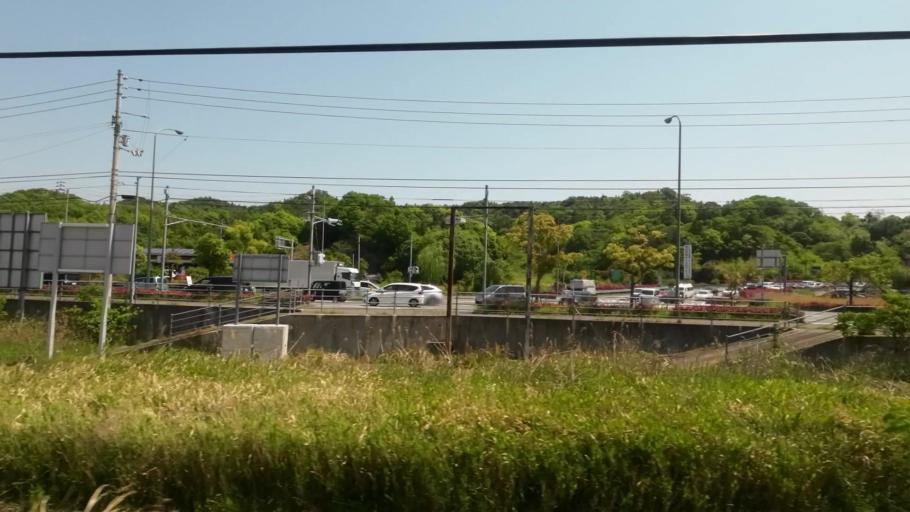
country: JP
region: Ehime
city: Saijo
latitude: 33.9965
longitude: 133.0431
